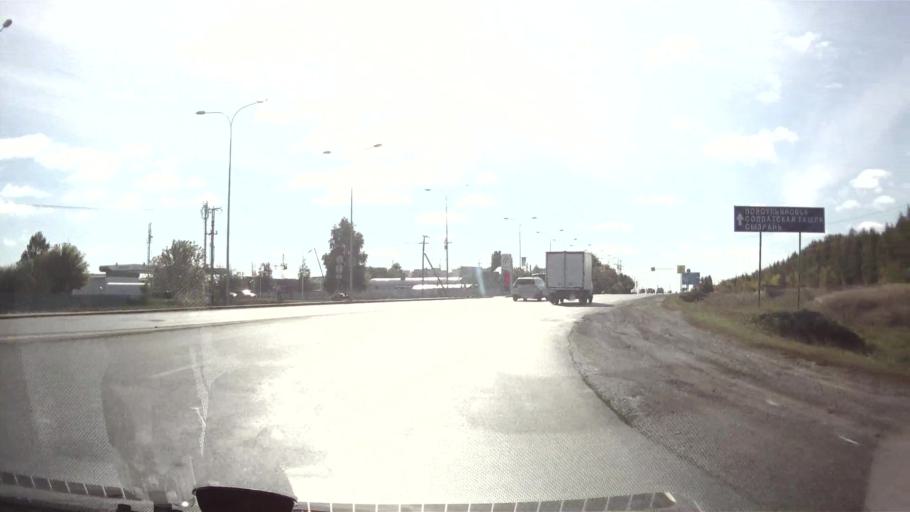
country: RU
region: Ulyanovsk
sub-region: Ulyanovskiy Rayon
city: Ulyanovsk
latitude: 54.2898
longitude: 48.2549
